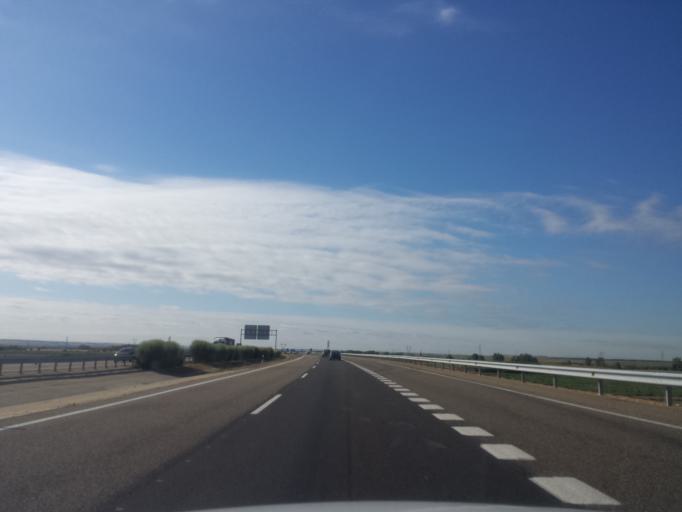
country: ES
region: Castille and Leon
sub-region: Provincia de Leon
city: Villamanan
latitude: 42.3227
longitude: -5.6080
